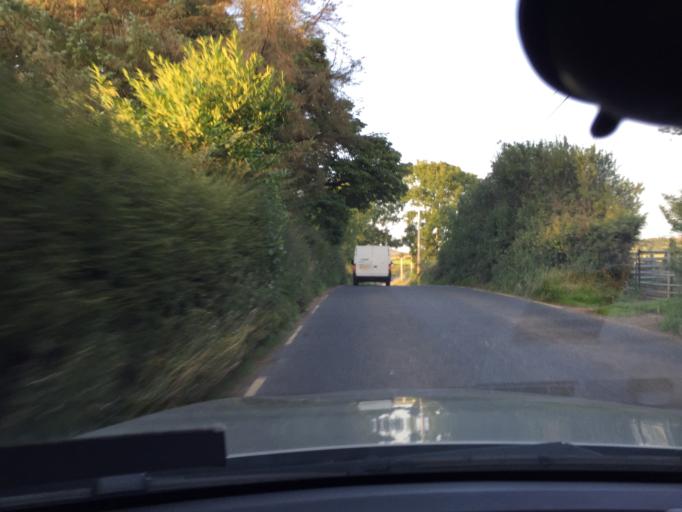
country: IE
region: Leinster
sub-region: Wicklow
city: Kilmacanoge
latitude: 53.1286
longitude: -6.1801
